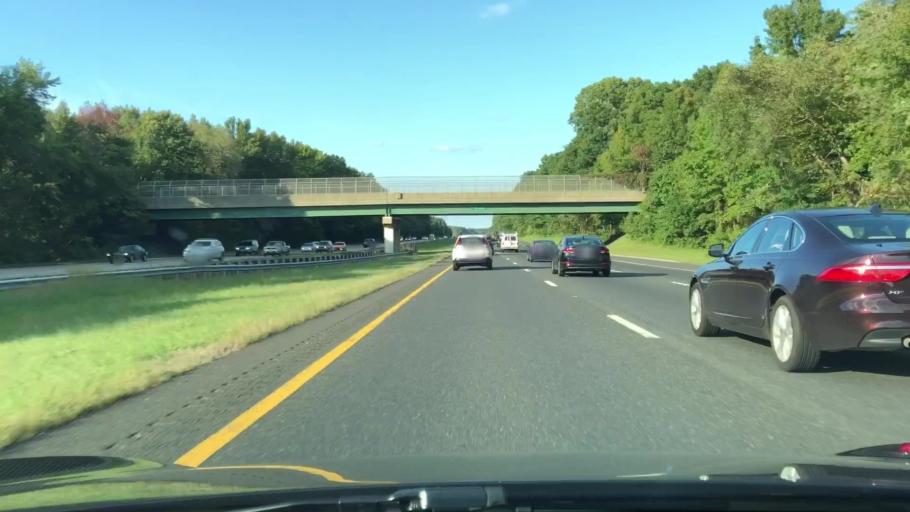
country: US
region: New Jersey
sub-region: Burlington County
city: Willingboro
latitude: 40.0212
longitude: -74.8449
